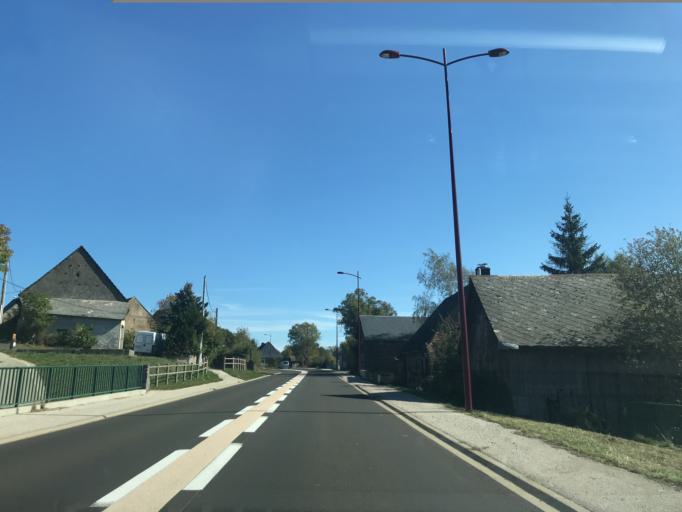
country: FR
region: Auvergne
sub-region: Departement du Puy-de-Dome
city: Gelles
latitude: 45.7330
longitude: 2.8346
